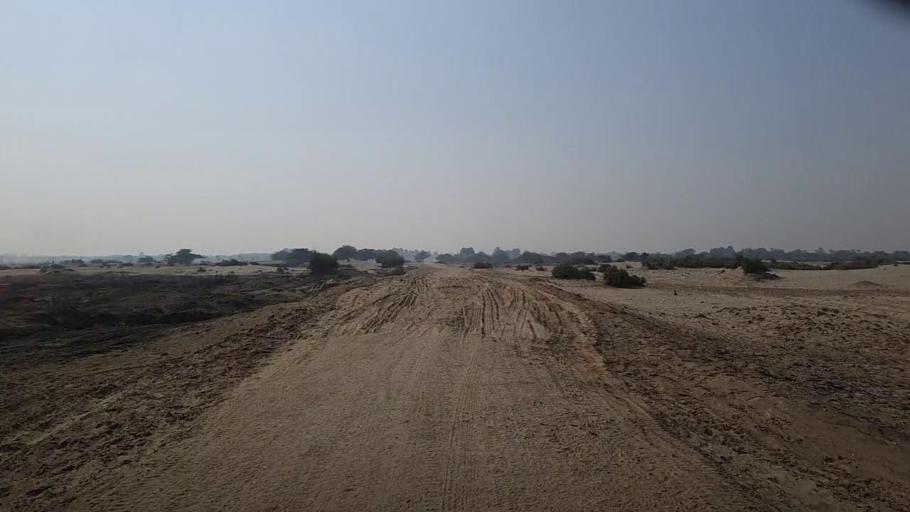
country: PK
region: Sindh
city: Bozdar
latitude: 27.2192
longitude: 68.5824
